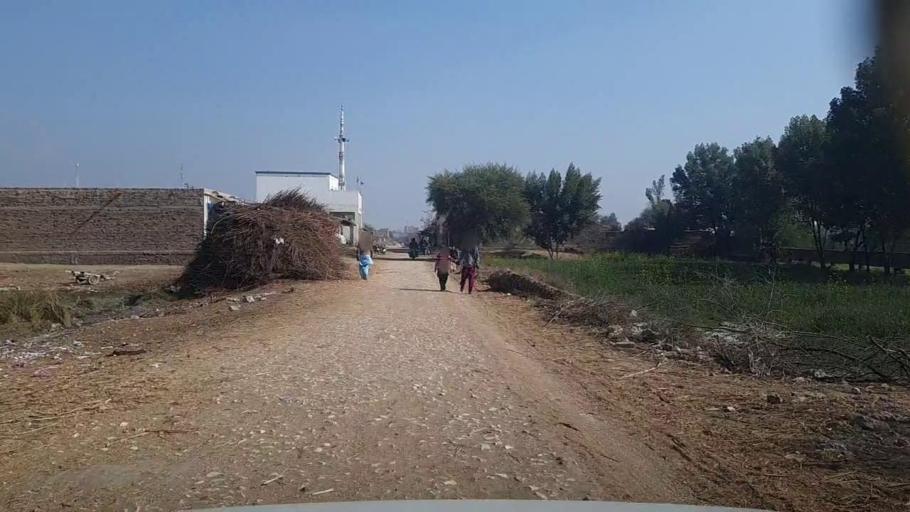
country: PK
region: Sindh
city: Khairpur
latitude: 27.9440
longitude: 69.6637
